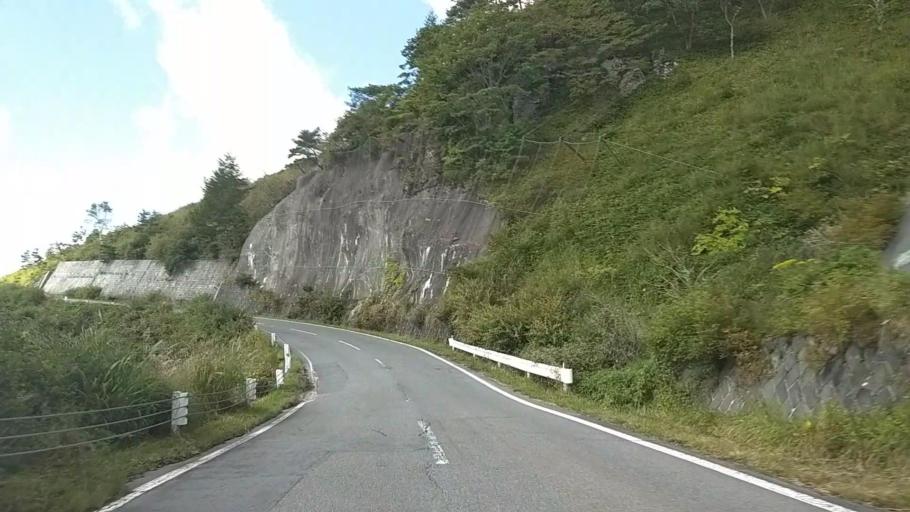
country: JP
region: Nagano
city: Suwa
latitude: 36.0944
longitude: 138.1933
